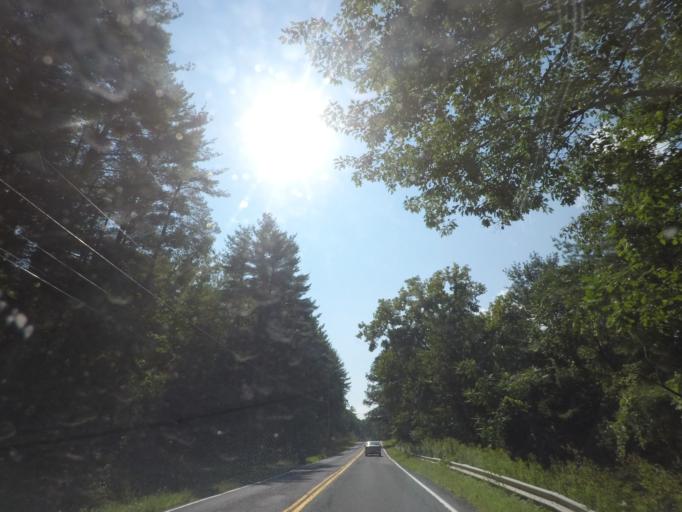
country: US
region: New York
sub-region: Rensselaer County
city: Poestenkill
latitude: 42.8219
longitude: -73.4910
